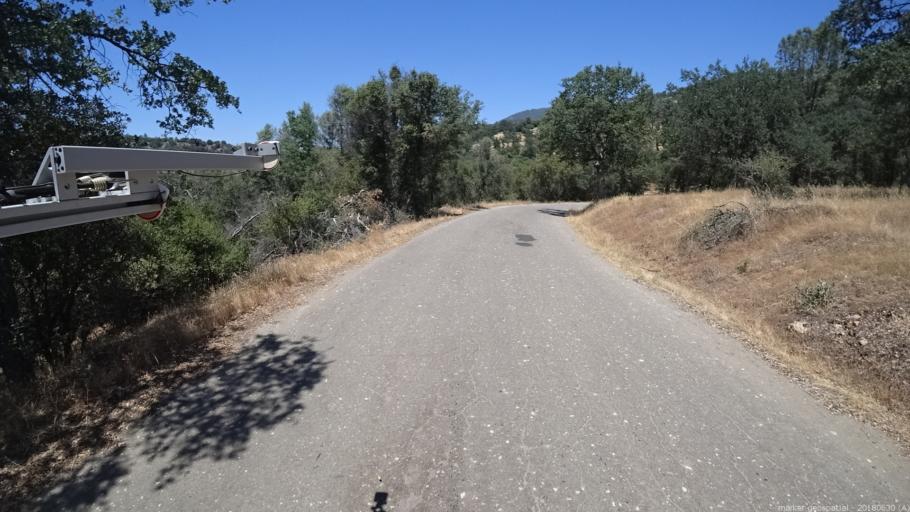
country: US
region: California
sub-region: Fresno County
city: Auberry
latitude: 37.1792
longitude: -119.4607
